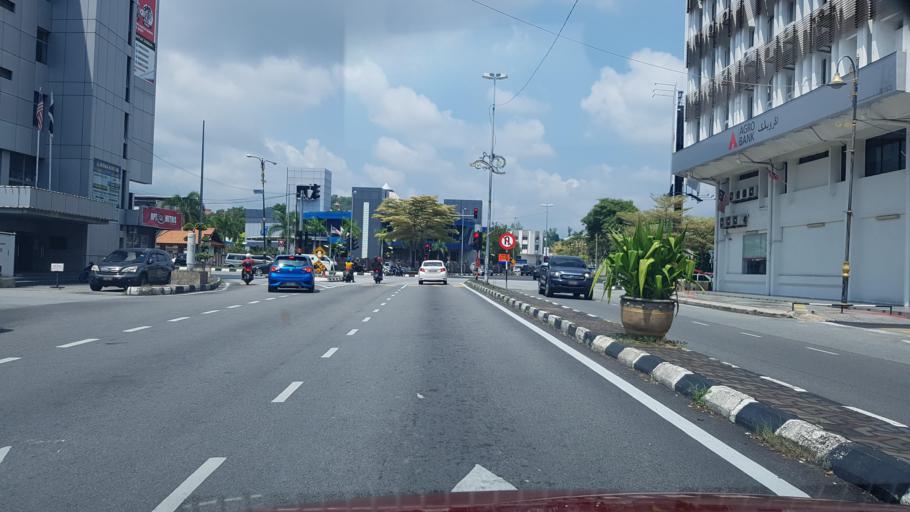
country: MY
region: Terengganu
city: Kuala Terengganu
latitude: 5.3300
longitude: 103.1381
